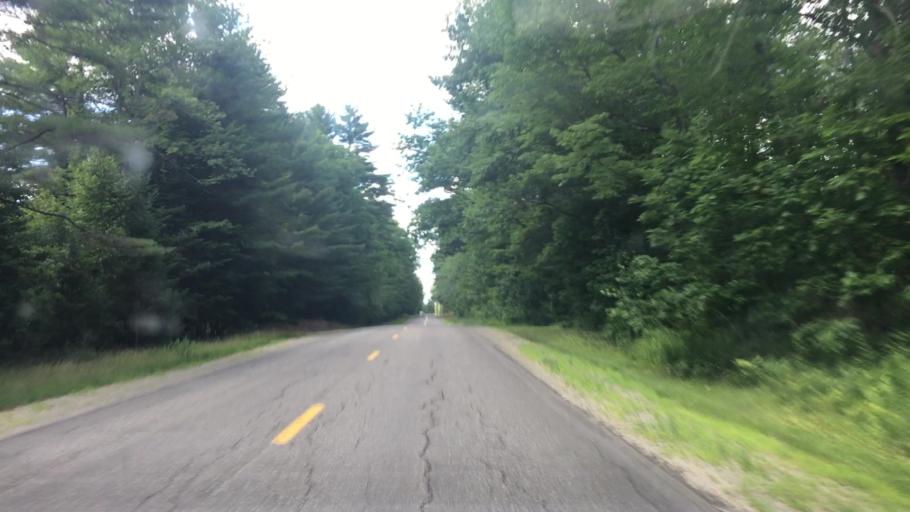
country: US
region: Maine
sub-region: Franklin County
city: Chesterville
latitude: 44.5982
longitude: -70.0849
